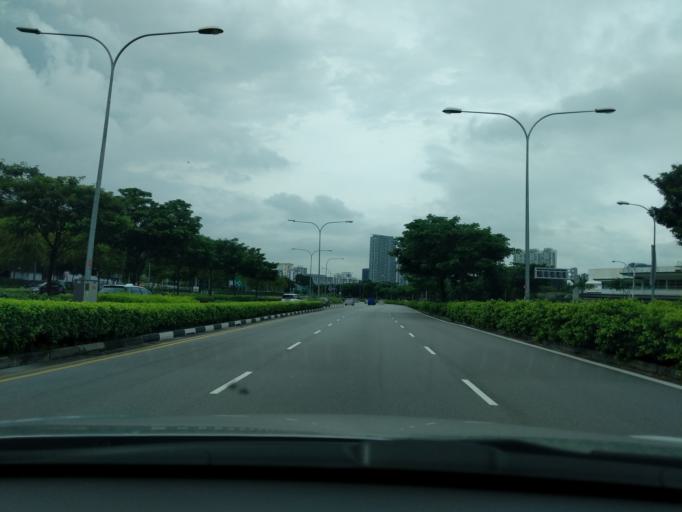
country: SG
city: Singapore
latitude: 1.3068
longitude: 103.8745
